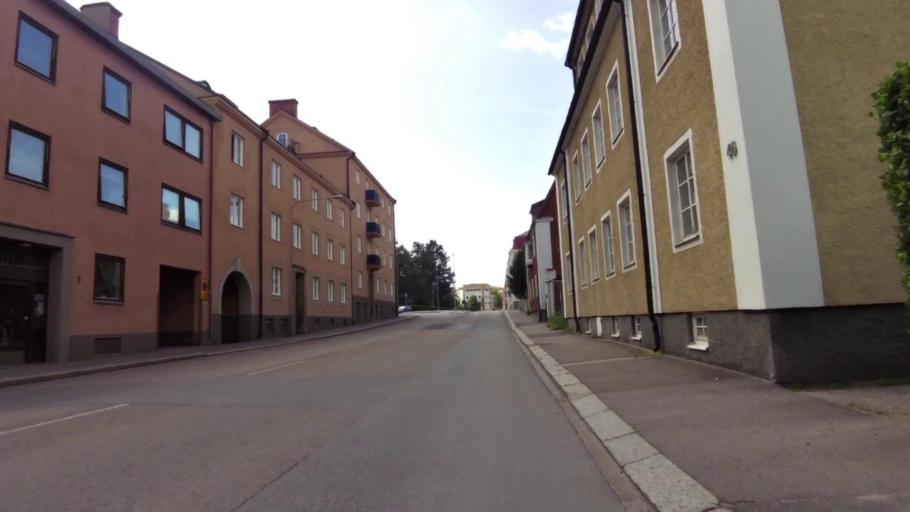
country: SE
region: OEstergoetland
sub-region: Linkopings Kommun
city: Linkoping
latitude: 58.4169
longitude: 15.6147
